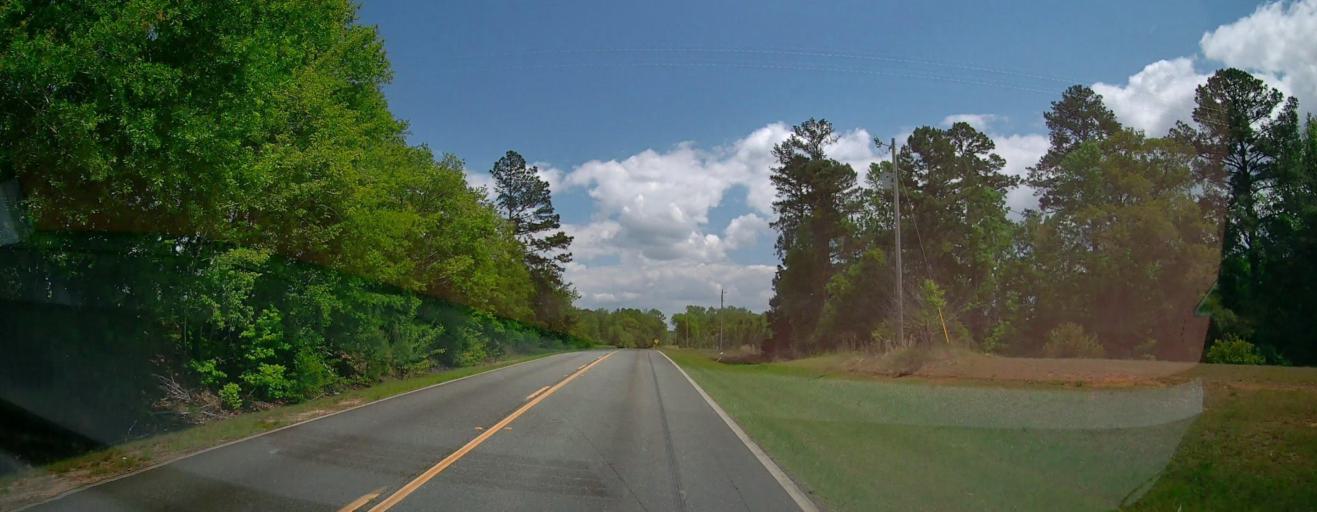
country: US
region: Georgia
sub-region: Treutlen County
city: Soperton
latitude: 32.5153
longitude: -82.6550
